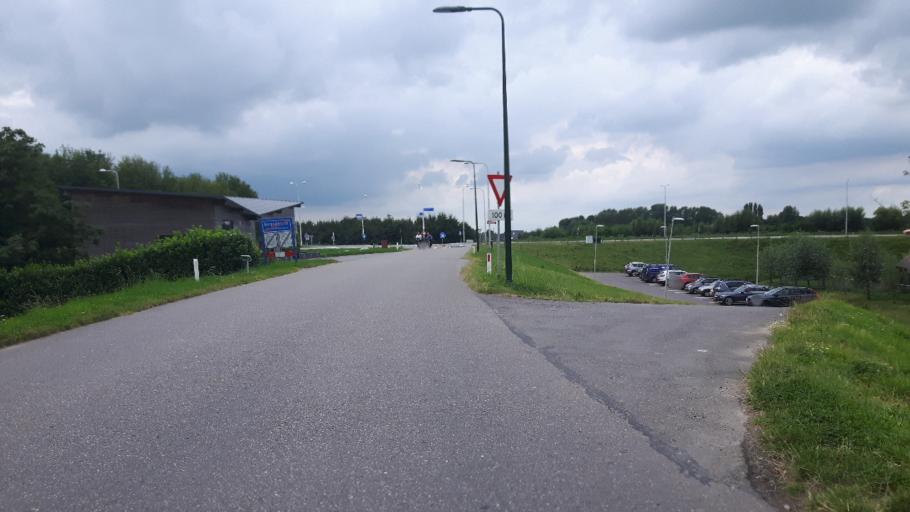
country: NL
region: South Holland
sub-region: Molenwaard
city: Liesveld
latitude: 51.9208
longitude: 4.7846
